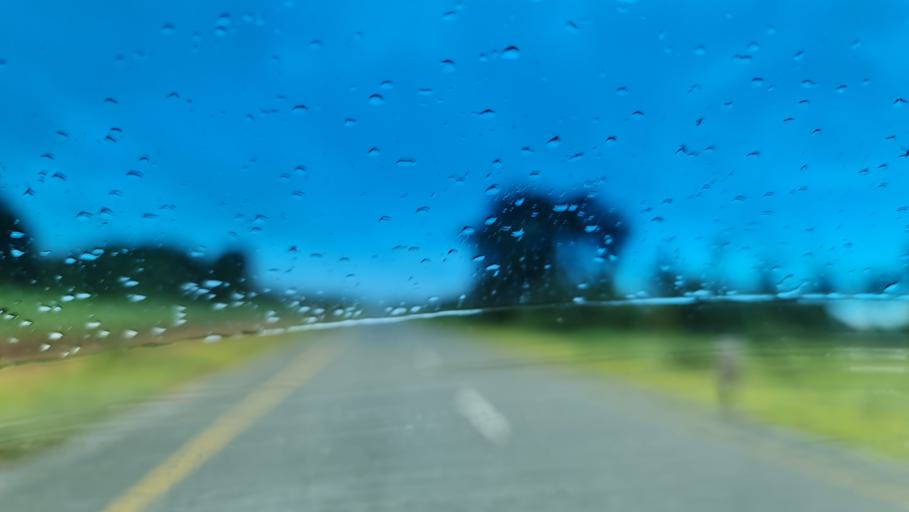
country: MZ
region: Nampula
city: Nampula
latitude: -15.5163
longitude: 39.3343
